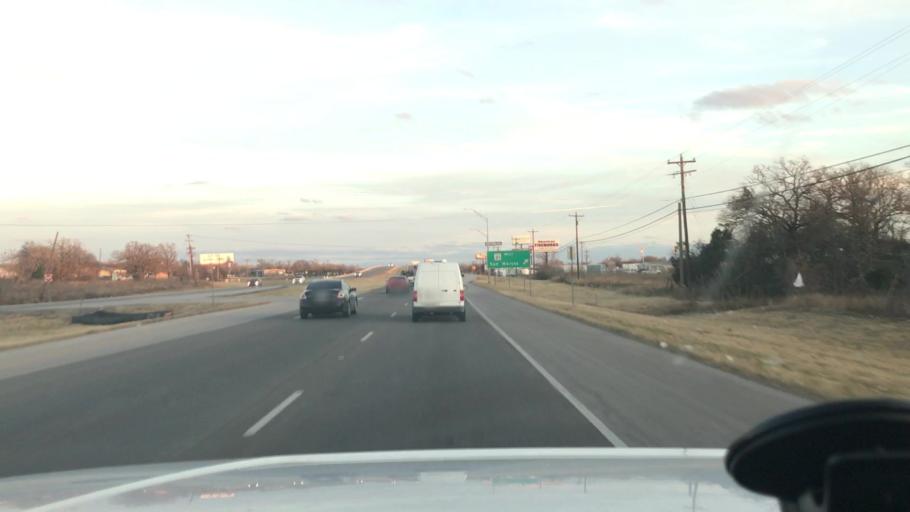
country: US
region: Texas
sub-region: Bastrop County
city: Wyldwood
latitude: 30.1159
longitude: -97.4218
